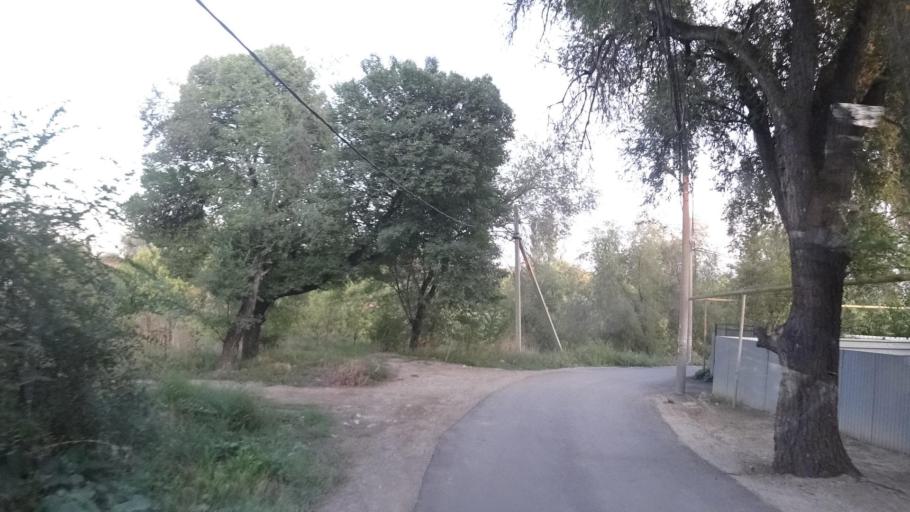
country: KZ
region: Almaty Oblysy
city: Pervomayskiy
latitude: 43.3390
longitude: 76.9976
